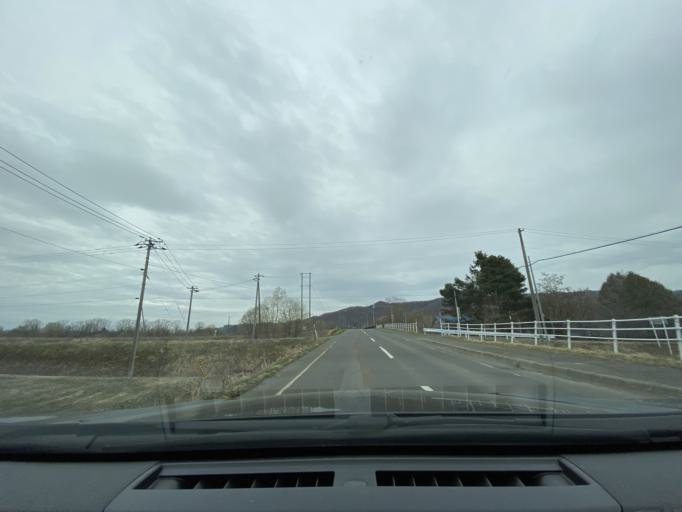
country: JP
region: Hokkaido
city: Nayoro
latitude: 44.1258
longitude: 142.4838
